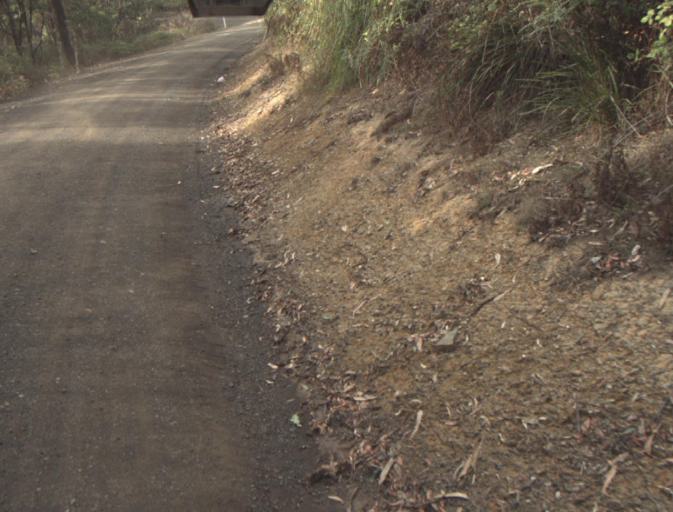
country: AU
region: Tasmania
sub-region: Launceston
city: Mayfield
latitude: -41.2140
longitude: 147.1776
